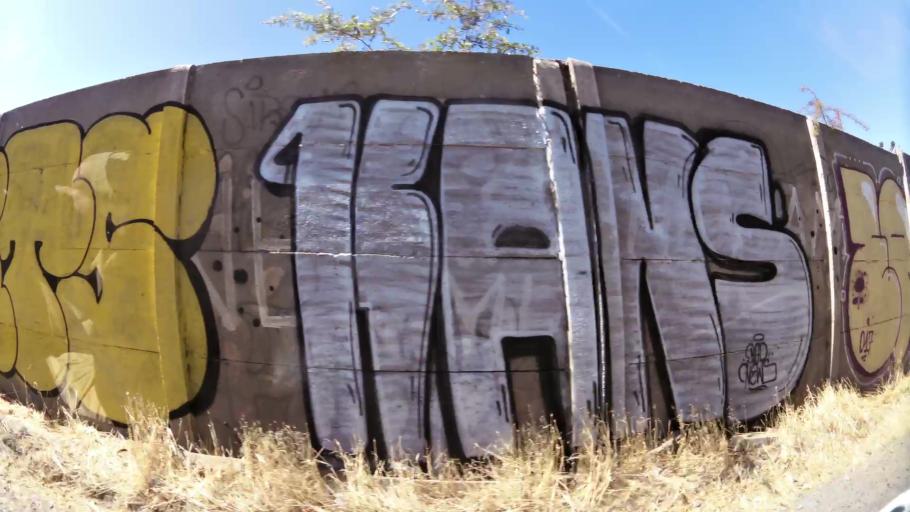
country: CL
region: O'Higgins
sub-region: Provincia de Cachapoal
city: Rancagua
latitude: -34.1593
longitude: -70.7543
